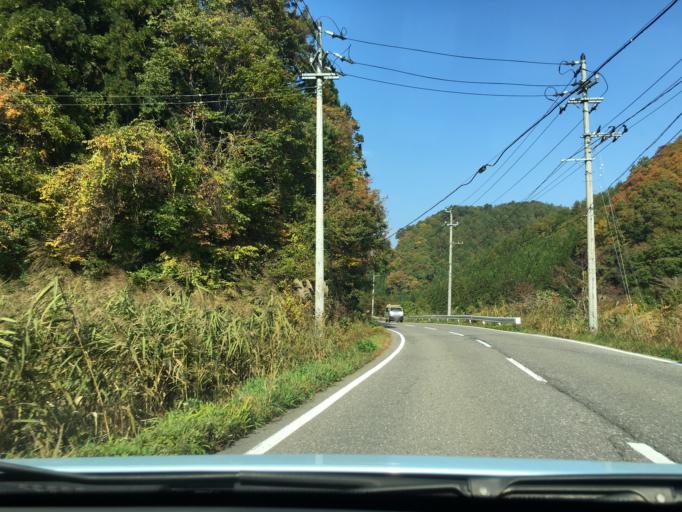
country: JP
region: Fukushima
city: Inawashiro
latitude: 37.4206
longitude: 140.0365
